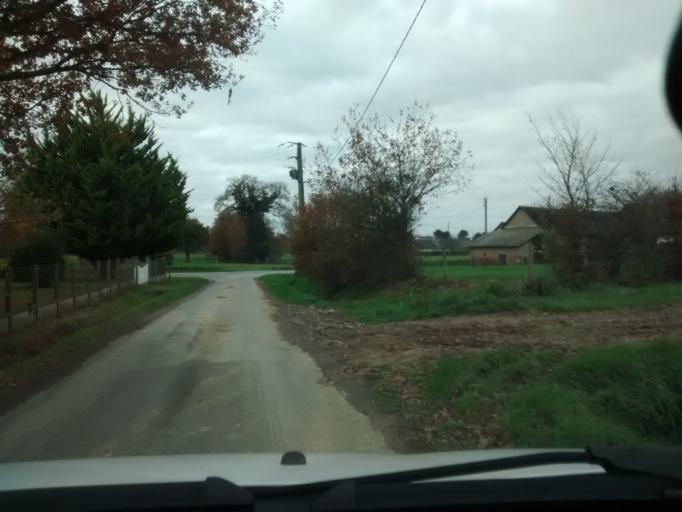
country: FR
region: Brittany
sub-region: Departement d'Ille-et-Vilaine
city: Le Rheu
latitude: 48.0870
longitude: -1.7697
